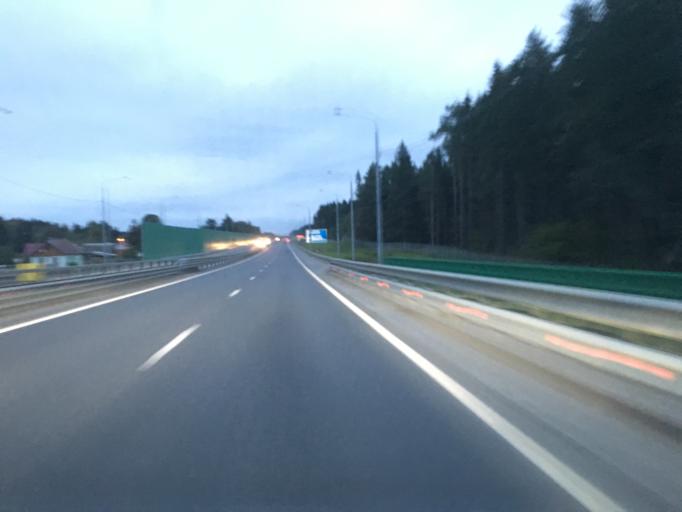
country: RU
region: Kaluga
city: Maloyaroslavets
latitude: 54.9168
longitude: 36.3929
